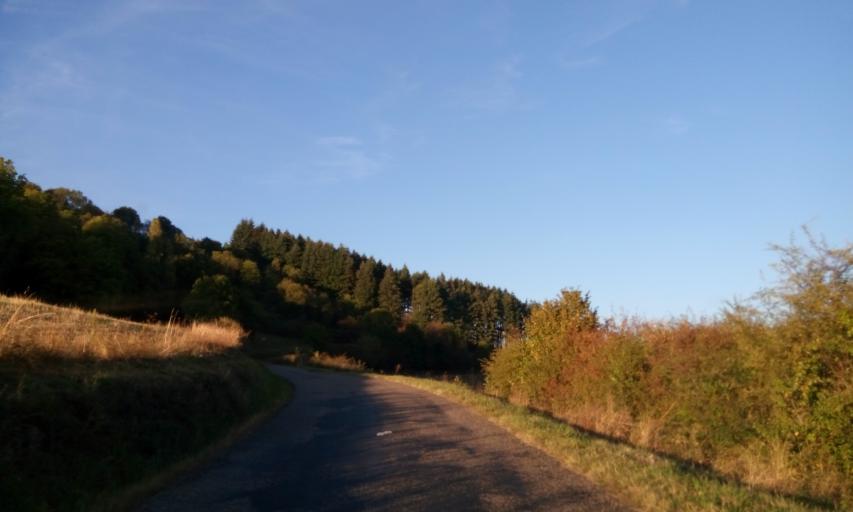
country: FR
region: Rhone-Alpes
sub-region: Departement du Rhone
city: Grandris
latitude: 45.9673
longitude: 4.4679
